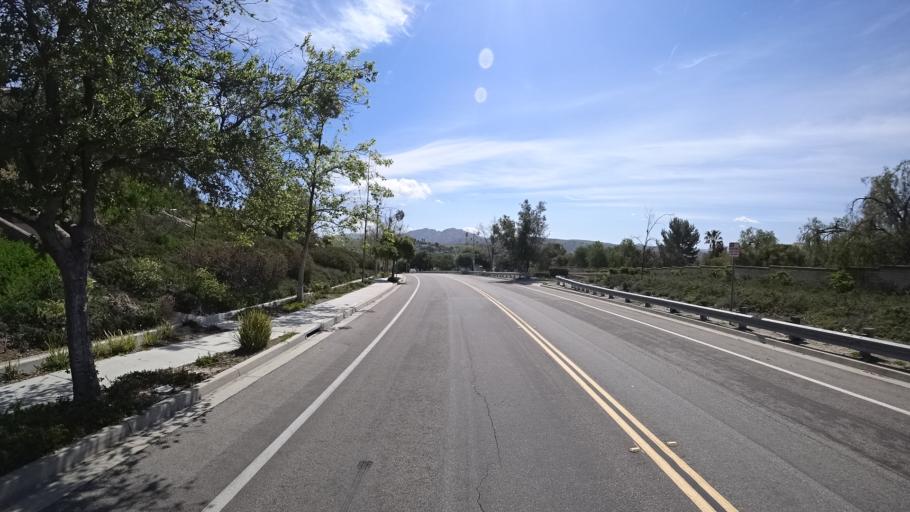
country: US
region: California
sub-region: Ventura County
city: Thousand Oaks
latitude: 34.2238
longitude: -118.8372
